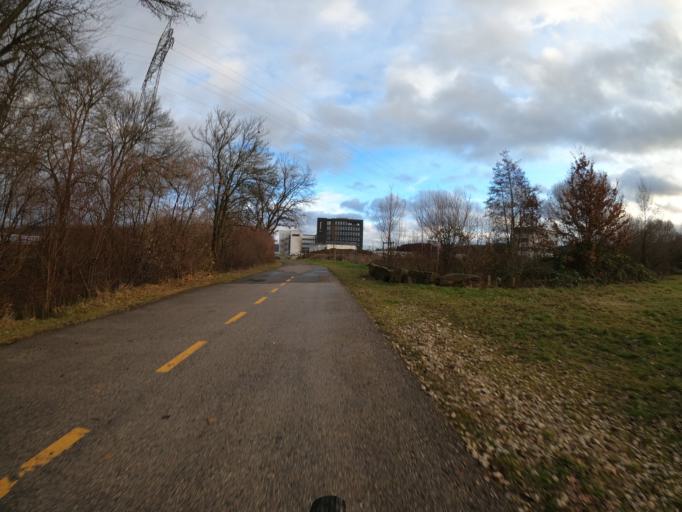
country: DE
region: Baden-Wuerttemberg
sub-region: Regierungsbezirk Stuttgart
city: Salach
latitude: 48.6882
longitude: 9.7228
